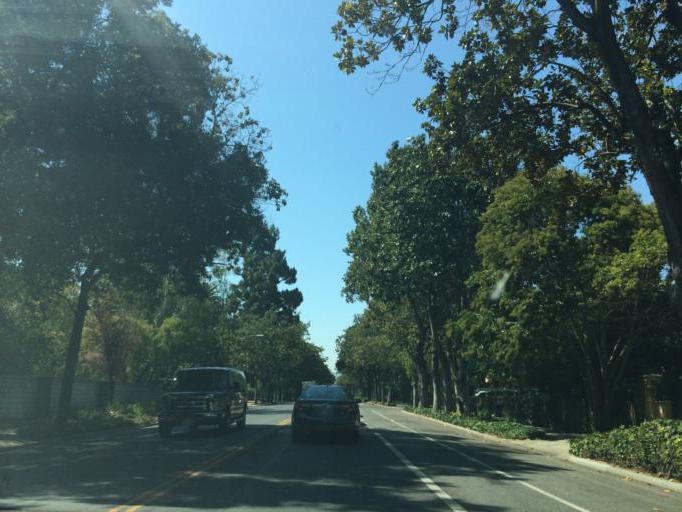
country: US
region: California
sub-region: Santa Clara County
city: Palo Alto
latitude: 37.4548
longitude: -122.1528
